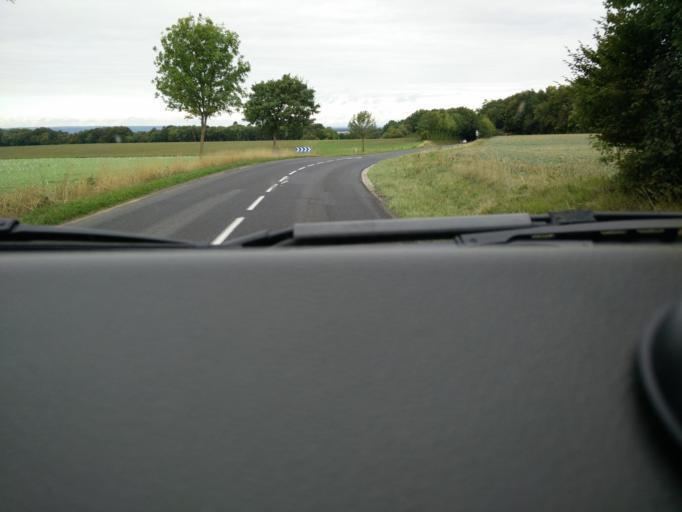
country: FR
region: Lorraine
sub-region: Departement de Meurthe-et-Moselle
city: Montauville
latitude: 48.9336
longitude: 5.8947
